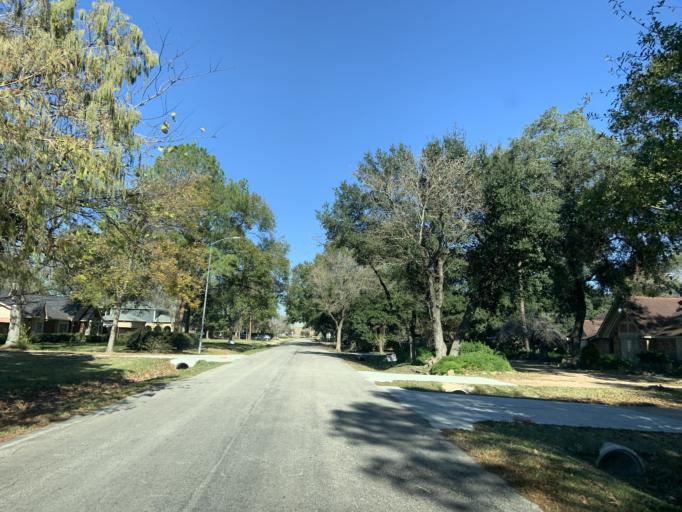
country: US
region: Texas
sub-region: Harris County
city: Bellaire
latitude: 29.6819
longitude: -95.5130
